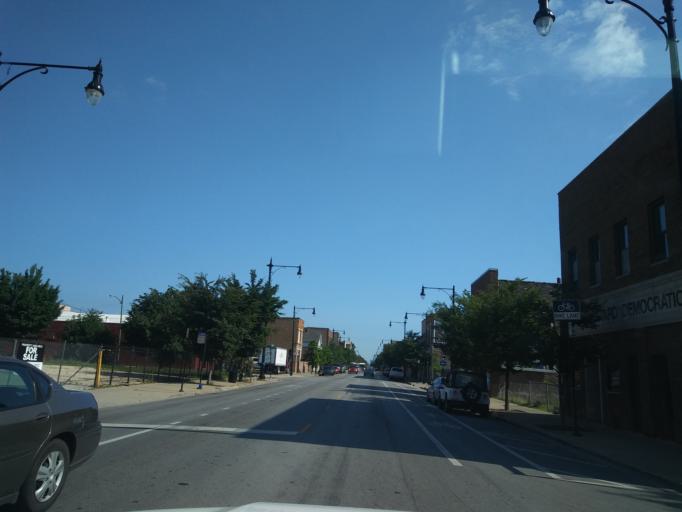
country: US
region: Illinois
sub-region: Cook County
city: Chicago
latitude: 41.8271
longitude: -87.6460
